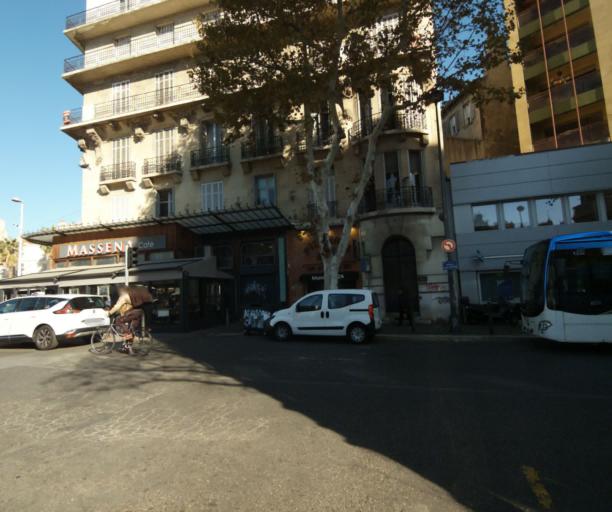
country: FR
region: Provence-Alpes-Cote d'Azur
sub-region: Departement des Bouches-du-Rhone
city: Marseille 06
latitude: 43.2855
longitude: 5.3844
